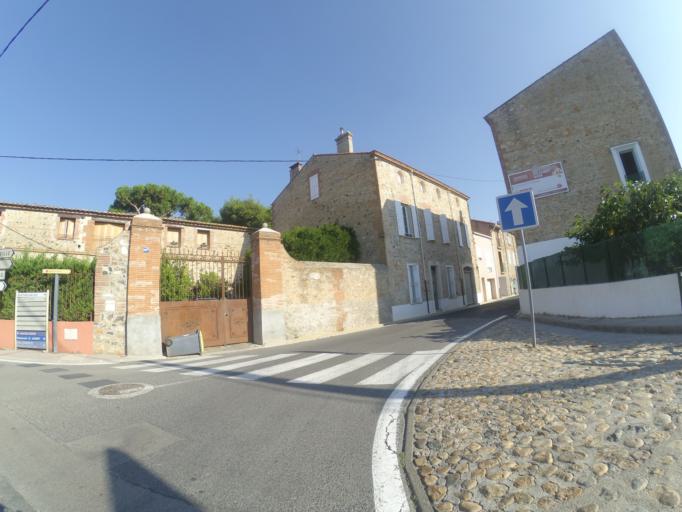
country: FR
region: Languedoc-Roussillon
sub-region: Departement des Pyrenees-Orientales
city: Peyrestortes
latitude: 42.7758
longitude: 2.8338
